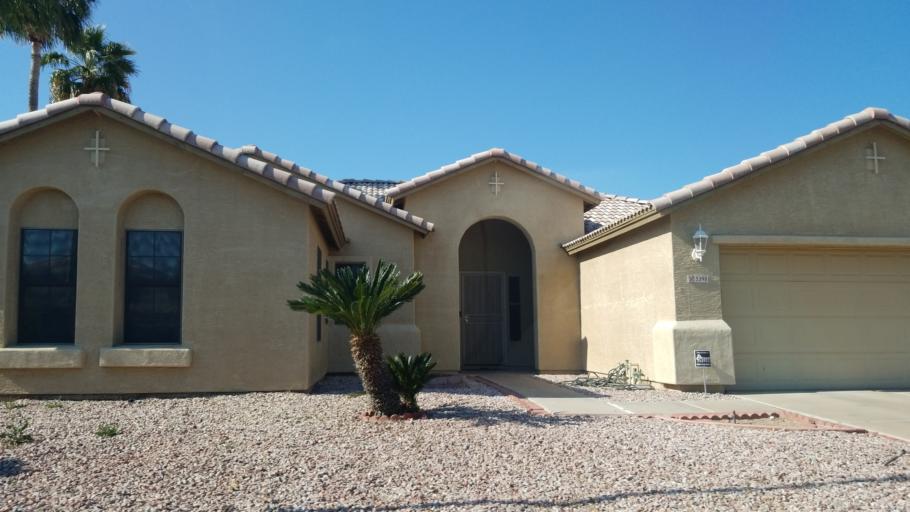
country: US
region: Arizona
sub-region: Maricopa County
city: Glendale
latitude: 33.5501
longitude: -112.1753
